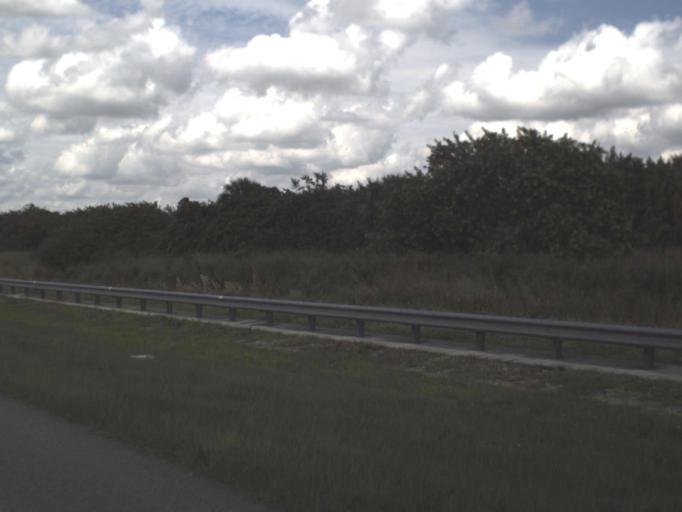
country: US
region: Florida
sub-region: Collier County
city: Immokalee
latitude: 26.3740
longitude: -81.3591
